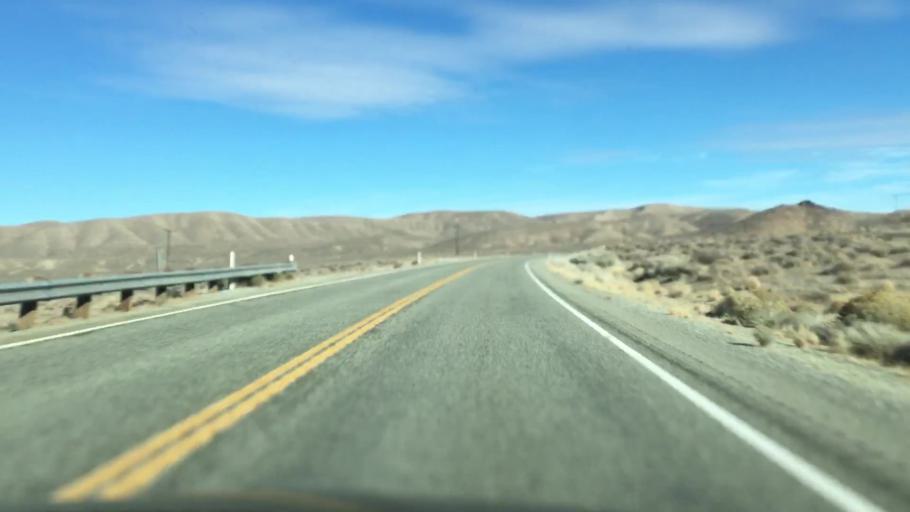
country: US
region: Nevada
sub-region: Lyon County
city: Yerington
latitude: 39.0455
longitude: -118.9765
